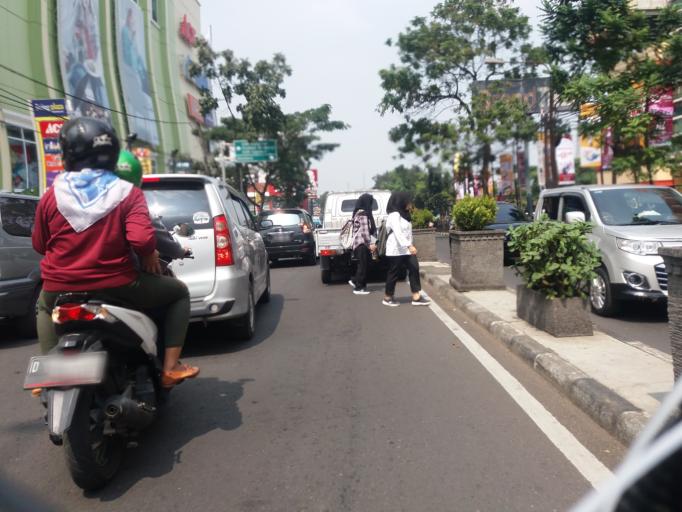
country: ID
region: West Java
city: Bandung
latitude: -6.9056
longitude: 107.5976
